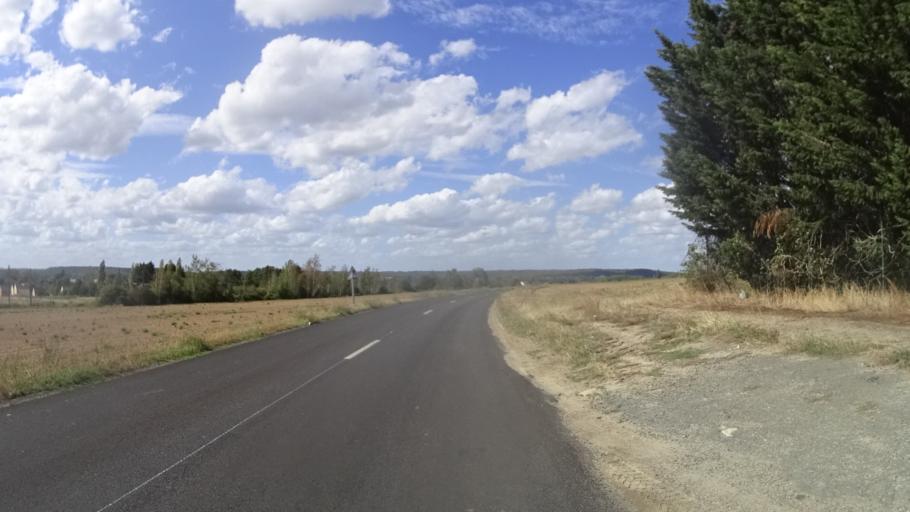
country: FR
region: Ile-de-France
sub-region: Departement de l'Essonne
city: La Ferte-Alais
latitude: 48.4591
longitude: 2.3545
